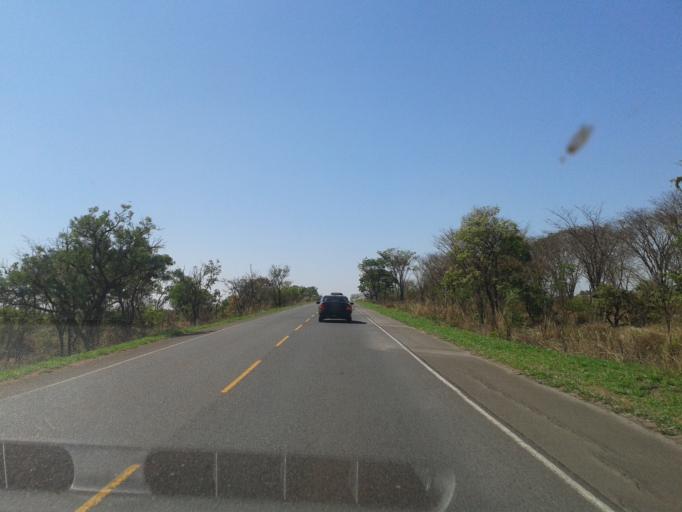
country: BR
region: Minas Gerais
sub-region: Uberlandia
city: Uberlandia
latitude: -19.0425
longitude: -48.0553
